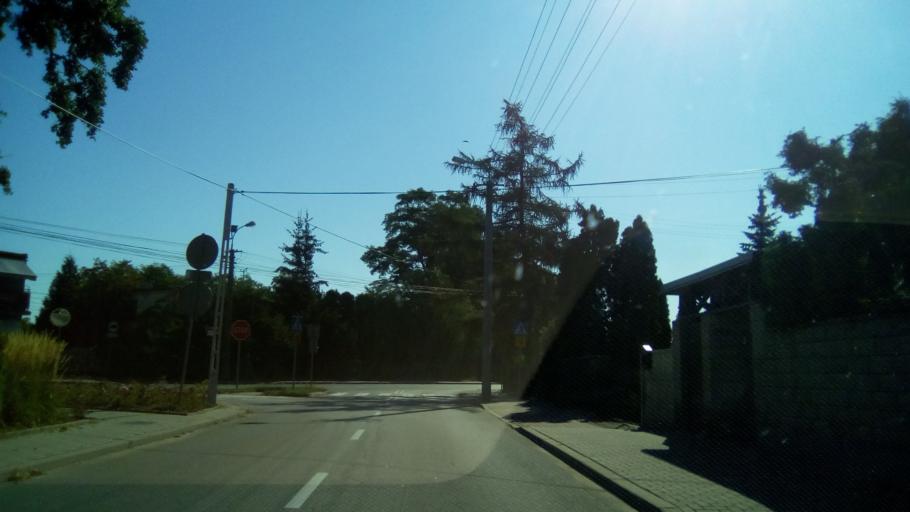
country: PL
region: Masovian Voivodeship
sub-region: Plock
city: Plock
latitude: 52.5261
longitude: 19.6804
